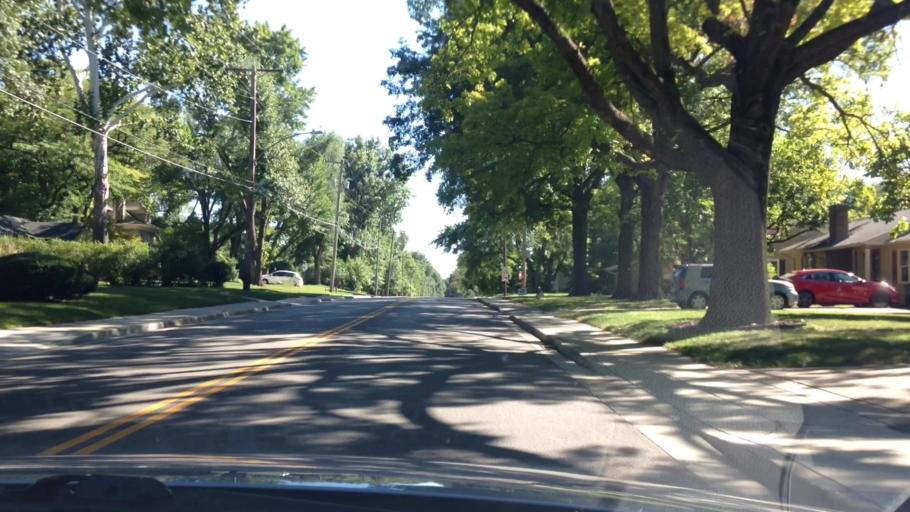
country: US
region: Kansas
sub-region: Johnson County
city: Fairway
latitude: 39.0232
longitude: -94.6304
